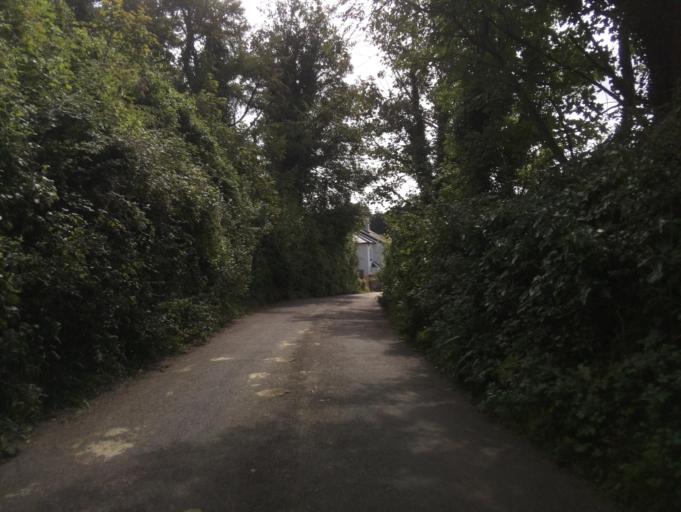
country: GB
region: England
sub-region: Borough of Torbay
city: Paignton
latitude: 50.3967
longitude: -3.5717
